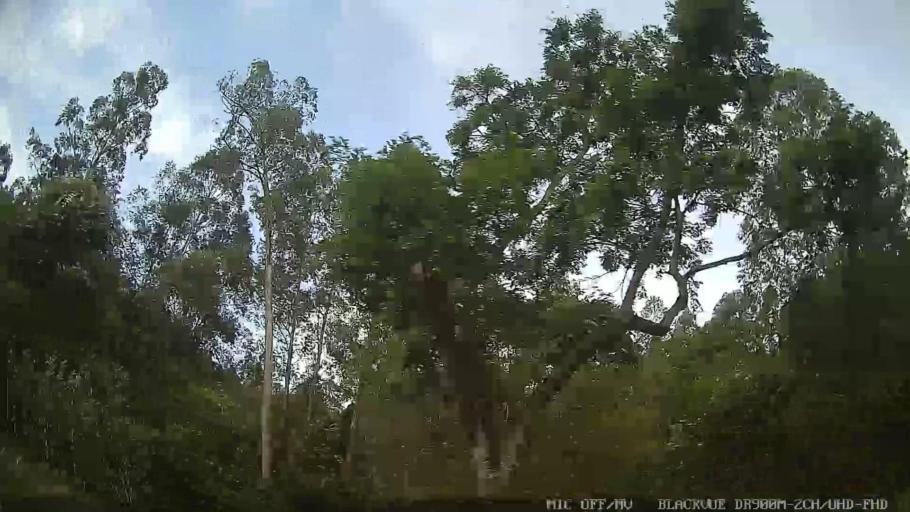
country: BR
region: Sao Paulo
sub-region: Amparo
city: Amparo
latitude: -22.7376
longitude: -46.7615
